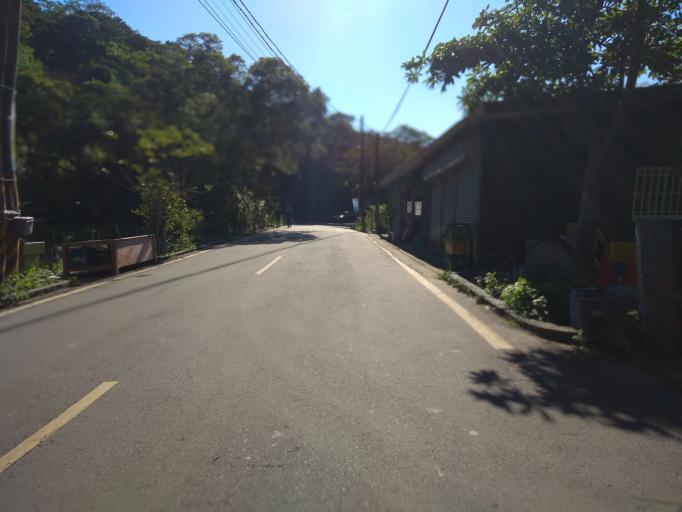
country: TW
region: Taiwan
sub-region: Hsinchu
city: Zhubei
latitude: 24.8605
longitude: 121.1044
